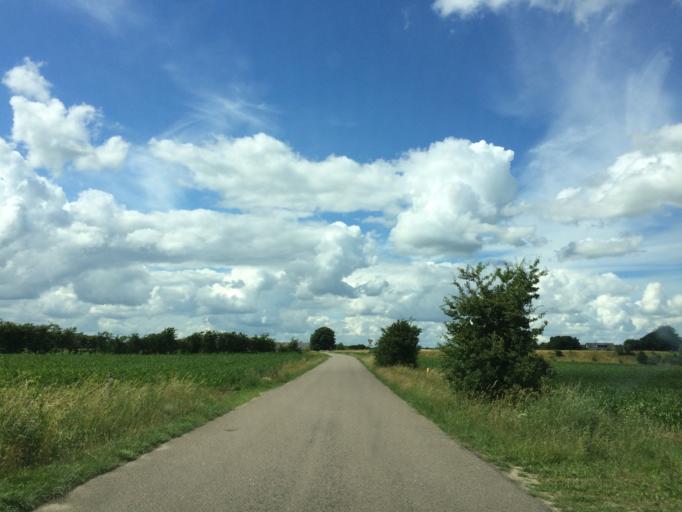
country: DK
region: North Denmark
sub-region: Vesthimmerland Kommune
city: Alestrup
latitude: 56.5673
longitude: 9.4908
